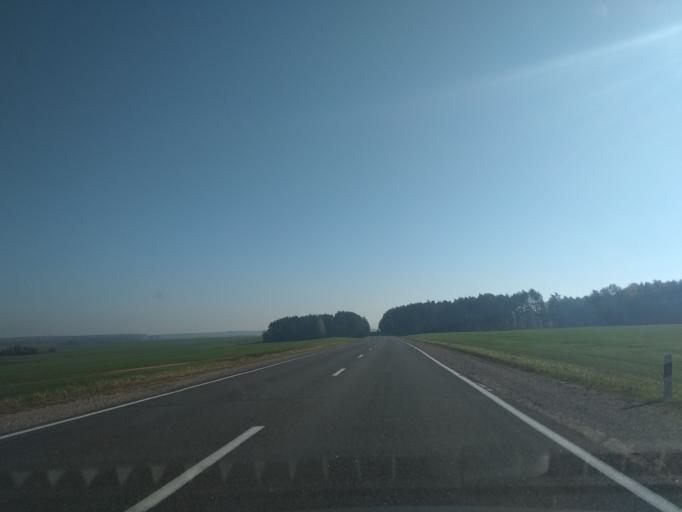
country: BY
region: Grodnenskaya
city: Zel'va
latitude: 53.1336
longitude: 24.9917
